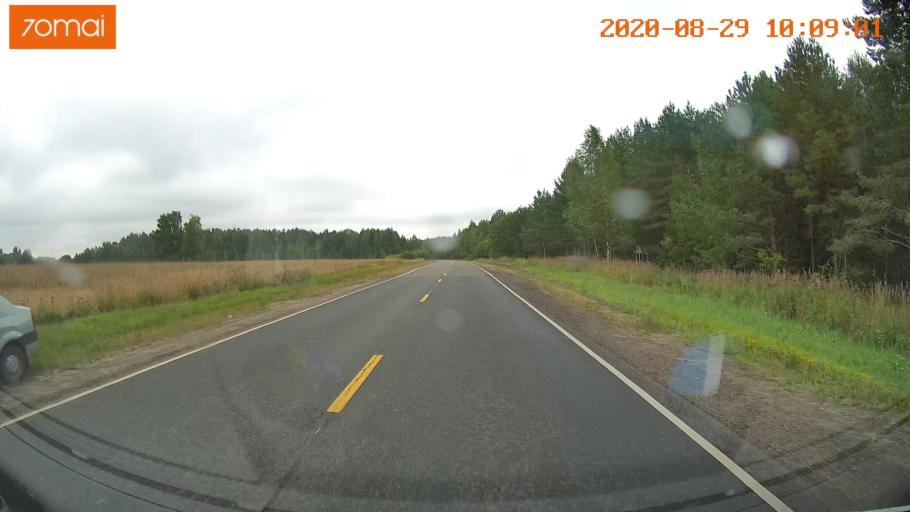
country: RU
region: Ivanovo
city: Kuznechikha
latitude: 57.3743
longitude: 42.6053
